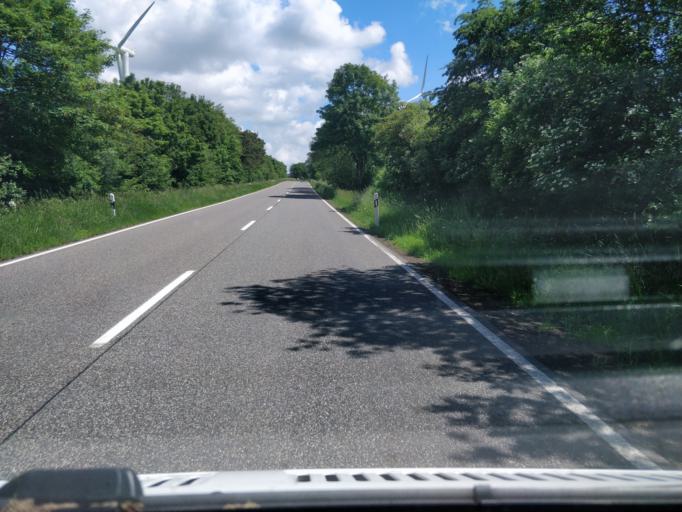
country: DE
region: Rheinland-Pfalz
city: Scheid
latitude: 50.3530
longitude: 6.3977
